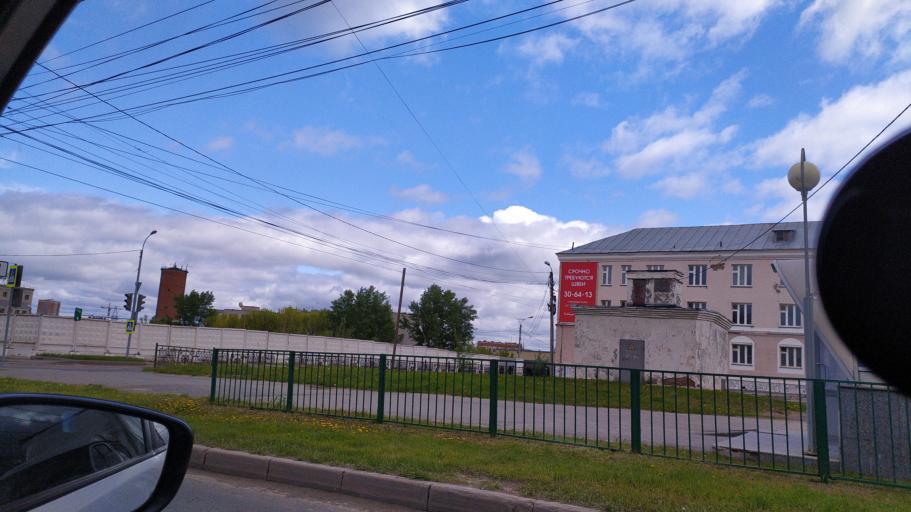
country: RU
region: Chuvashia
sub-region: Cheboksarskiy Rayon
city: Cheboksary
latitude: 56.1348
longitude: 47.2808
